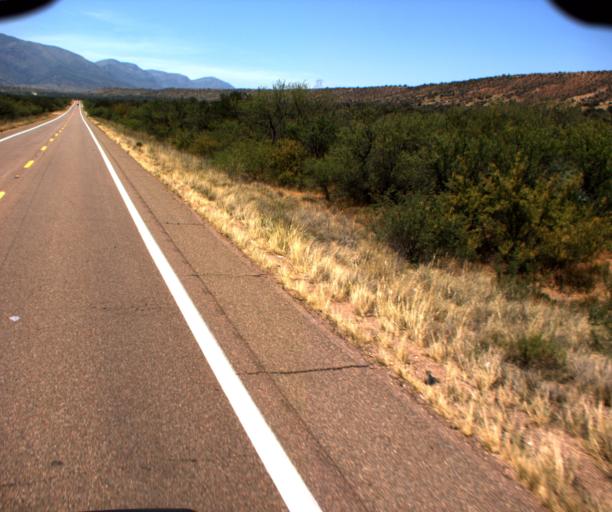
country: US
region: Arizona
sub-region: Gila County
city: Tonto Basin
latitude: 34.0195
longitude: -111.3341
